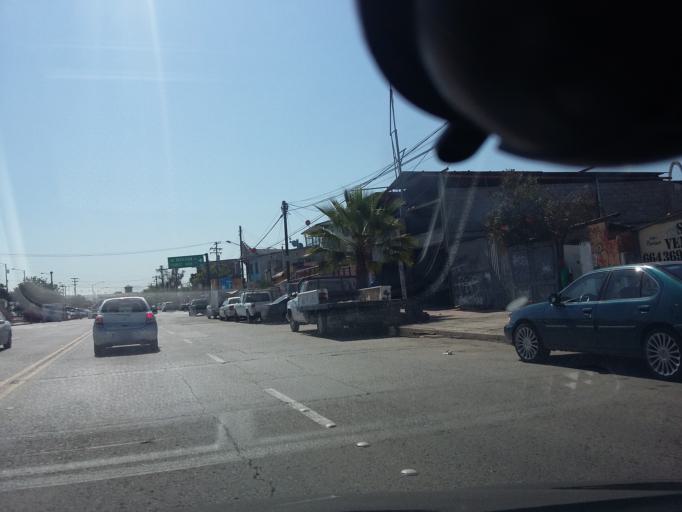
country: MX
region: Baja California
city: Tijuana
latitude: 32.5404
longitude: -117.0383
